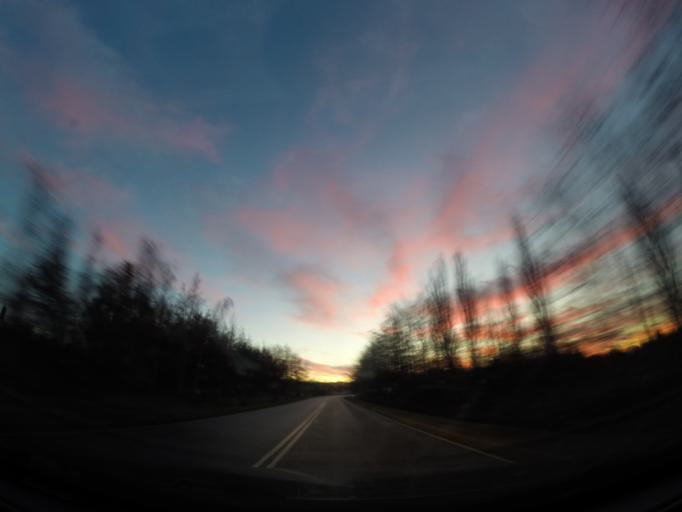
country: DK
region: Capital Region
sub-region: Hoje-Taastrup Kommune
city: Taastrup
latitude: 55.6694
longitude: 12.2867
